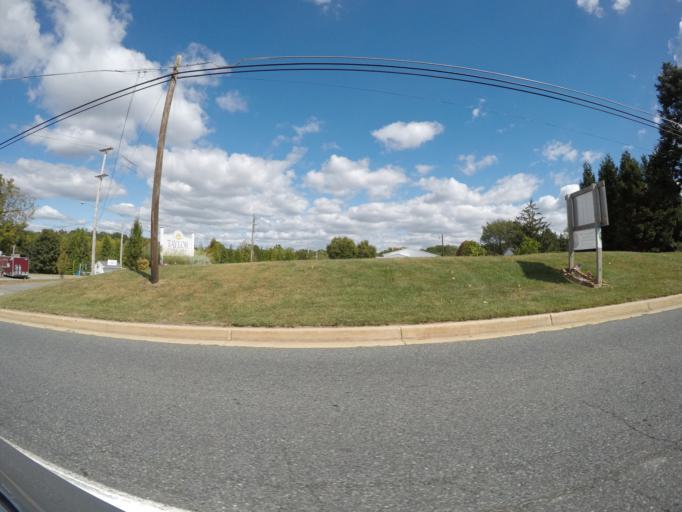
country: US
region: Pennsylvania
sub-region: York County
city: Susquehanna Trails
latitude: 39.7107
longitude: -76.3481
